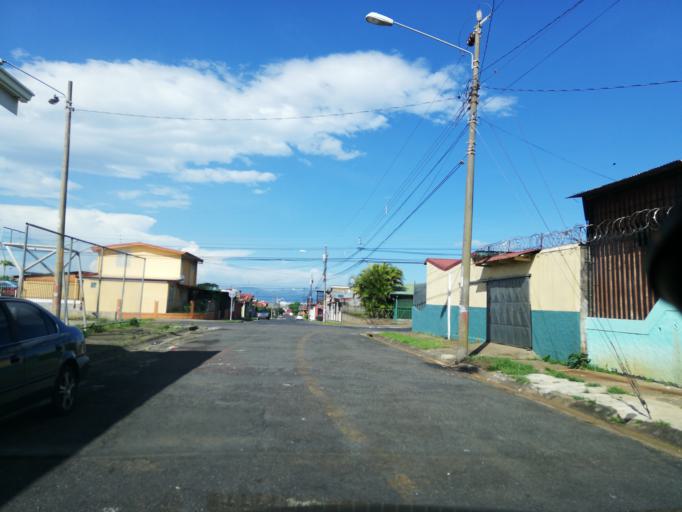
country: CR
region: Alajuela
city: Alajuela
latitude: 10.0066
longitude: -84.2037
